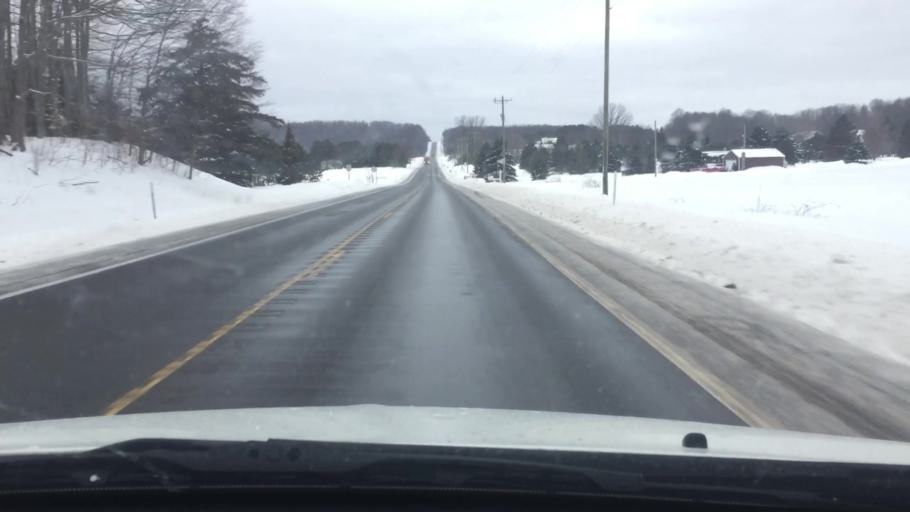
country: US
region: Michigan
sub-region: Charlevoix County
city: Boyne City
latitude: 45.0965
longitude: -84.9876
